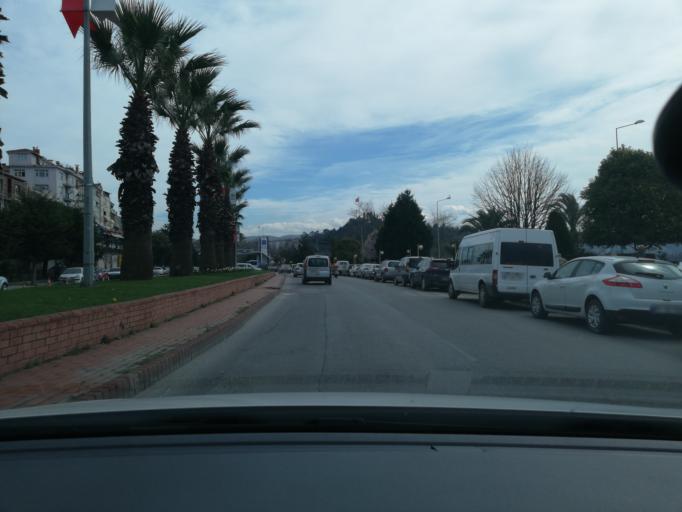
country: TR
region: Zonguldak
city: Eregli
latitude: 41.2817
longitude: 31.4162
